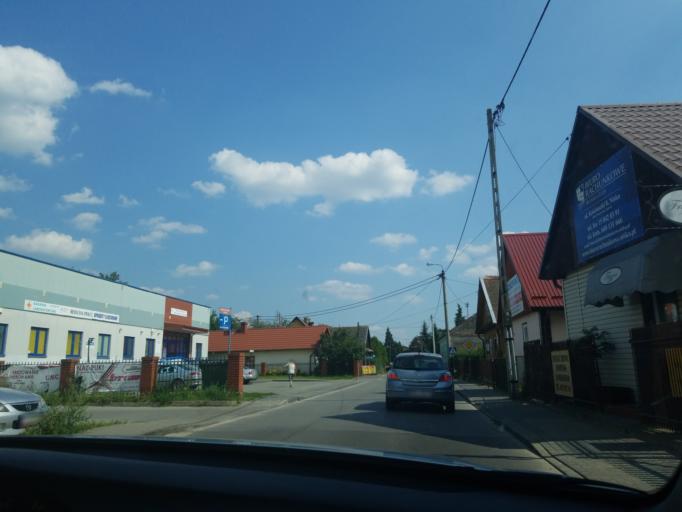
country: PL
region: Subcarpathian Voivodeship
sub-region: Powiat nizanski
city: Nisko
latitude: 50.5178
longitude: 22.1399
